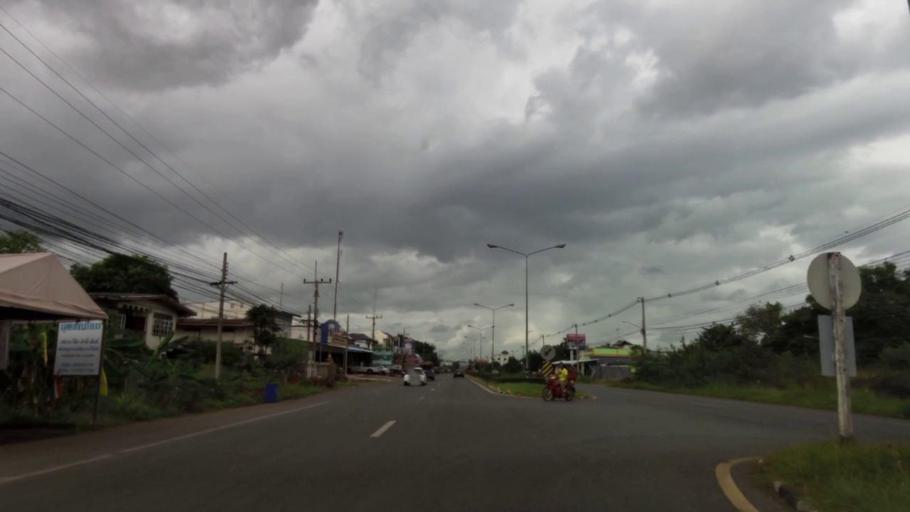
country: TH
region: Nakhon Sawan
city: Phai Sali
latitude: 15.5934
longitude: 100.6519
